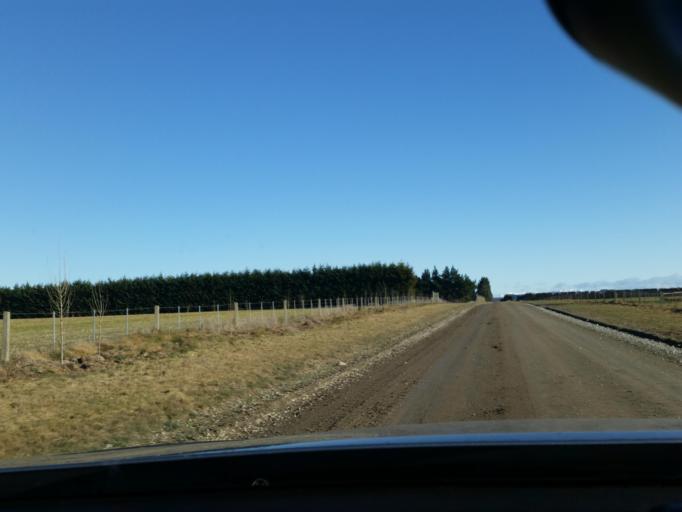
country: NZ
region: Southland
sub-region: Gore District
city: Gore
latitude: -45.7915
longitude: 168.6948
